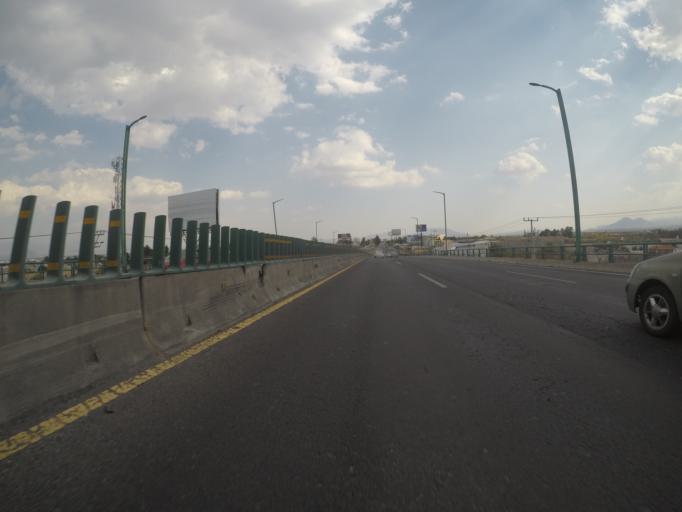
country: MX
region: Morelos
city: San Miguel Totocuitlapilco
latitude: 19.2350
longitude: -99.5977
